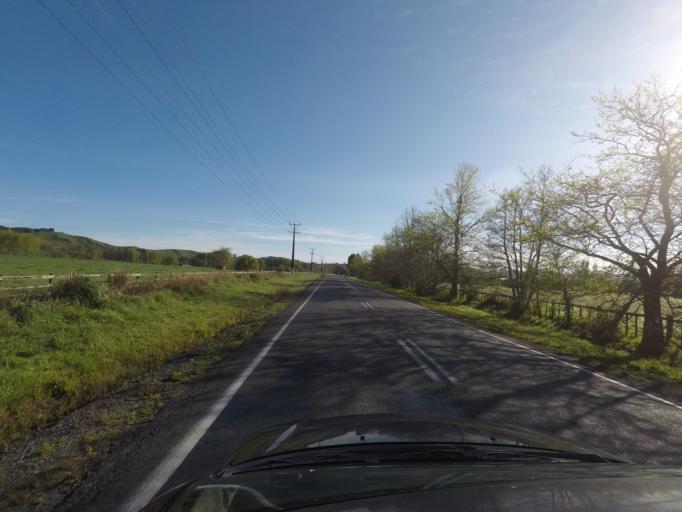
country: NZ
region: Auckland
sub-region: Auckland
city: Red Hill
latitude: -37.0078
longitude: 174.9534
